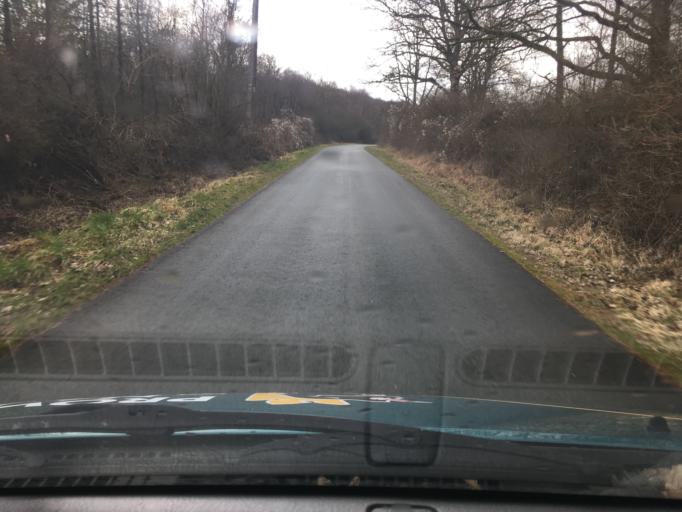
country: BE
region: Wallonia
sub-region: Province de Namur
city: Couvin
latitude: 50.0579
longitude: 4.5559
